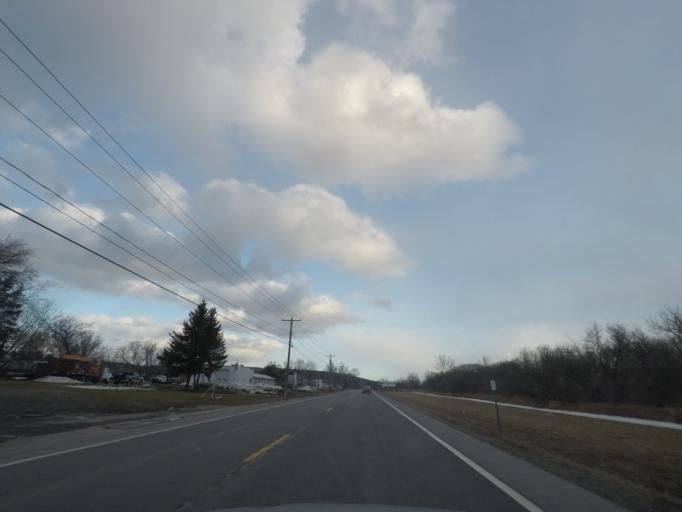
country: US
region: New York
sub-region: Herkimer County
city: Frankfort
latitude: 43.0605
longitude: -75.0855
